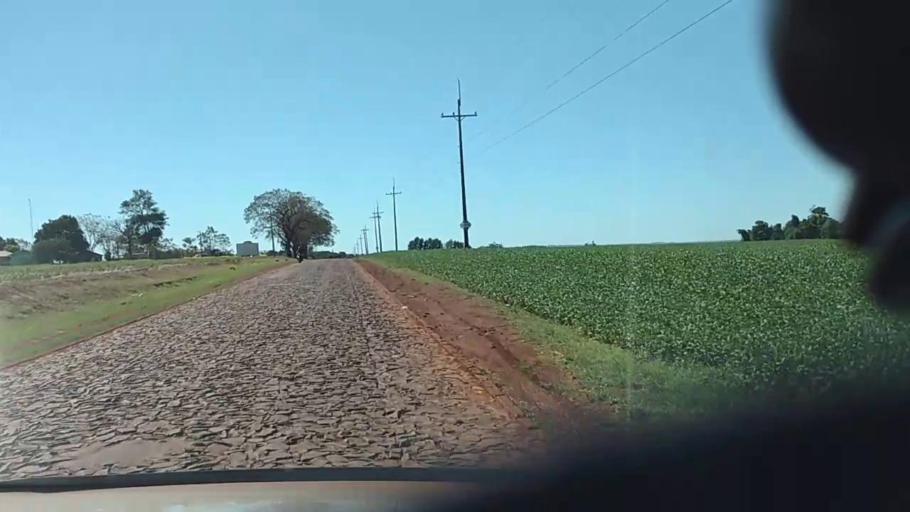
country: PY
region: Alto Parana
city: Naranjal
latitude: -25.9557
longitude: -55.1349
